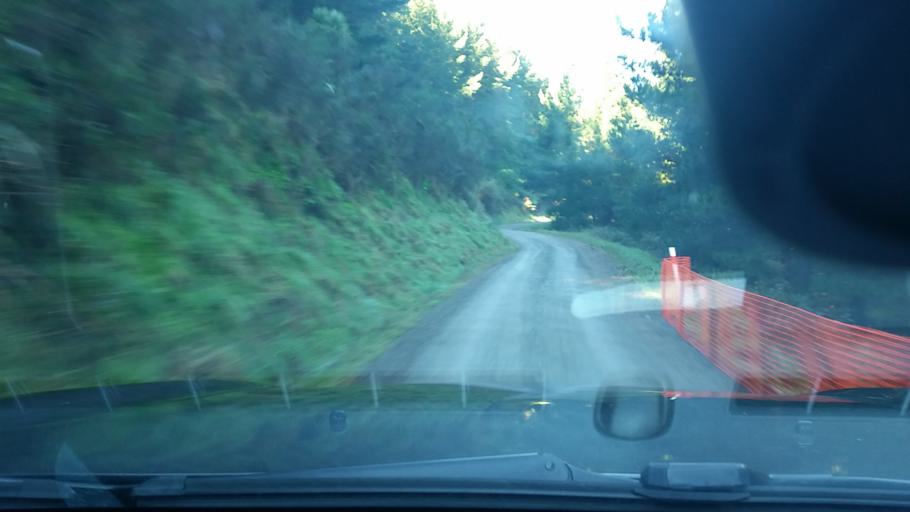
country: NZ
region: Marlborough
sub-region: Marlborough District
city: Blenheim
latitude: -41.6240
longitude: 173.9653
